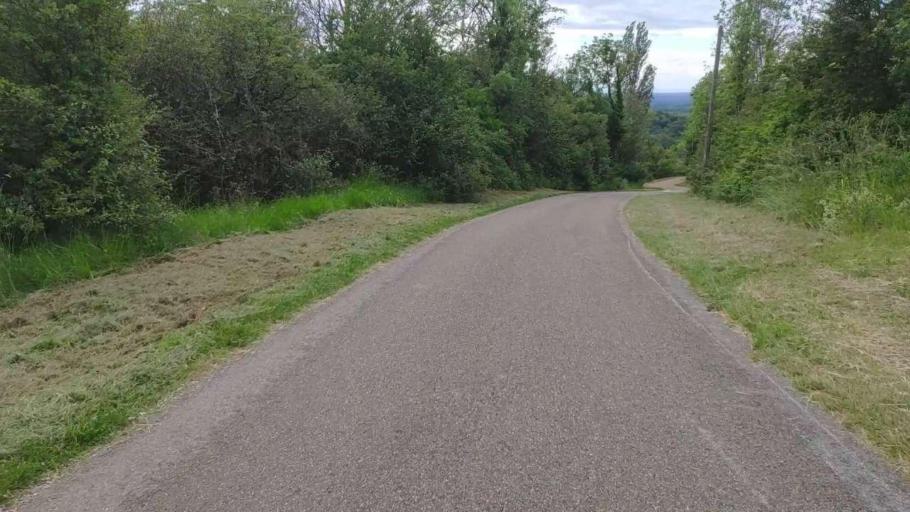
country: FR
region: Franche-Comte
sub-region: Departement du Jura
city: Perrigny
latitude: 46.7831
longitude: 5.5685
